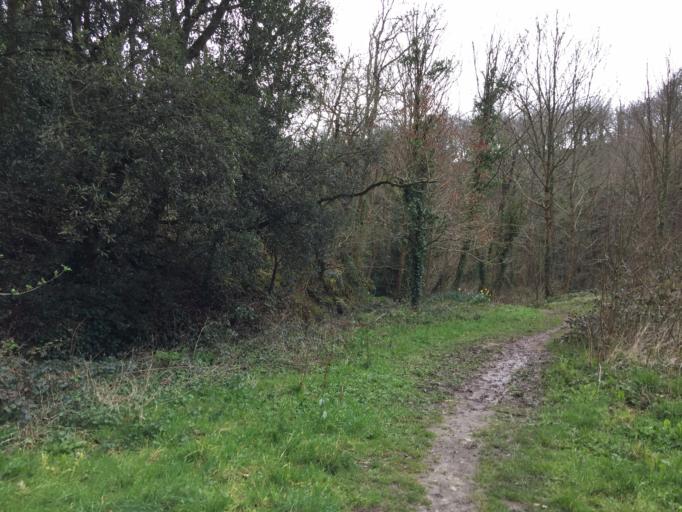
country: JE
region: St Helier
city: Saint Helier
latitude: 49.2129
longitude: -2.1340
